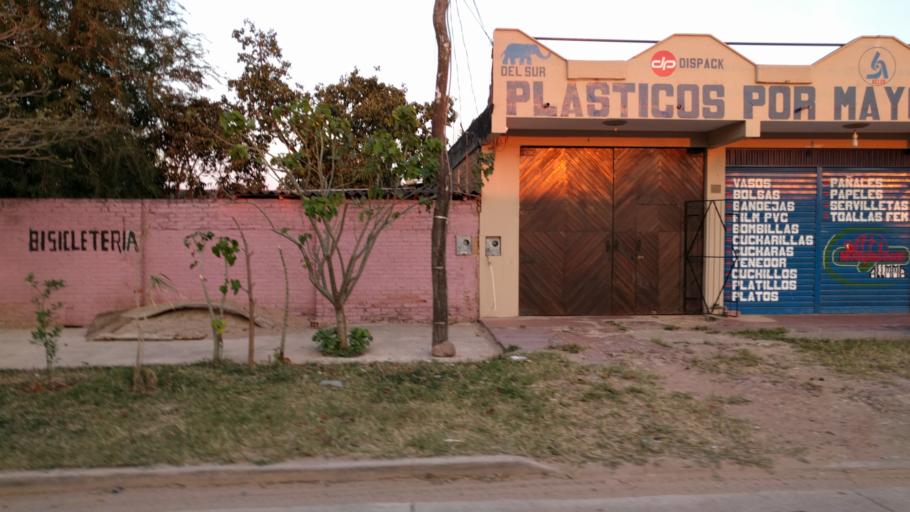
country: BO
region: Santa Cruz
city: Santa Cruz de la Sierra
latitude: -17.7525
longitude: -63.1496
